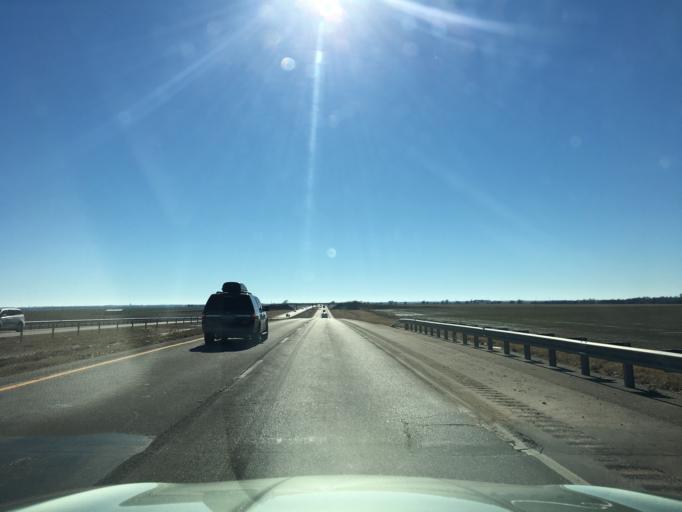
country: US
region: Oklahoma
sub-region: Kay County
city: Blackwell
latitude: 36.7736
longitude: -97.3461
